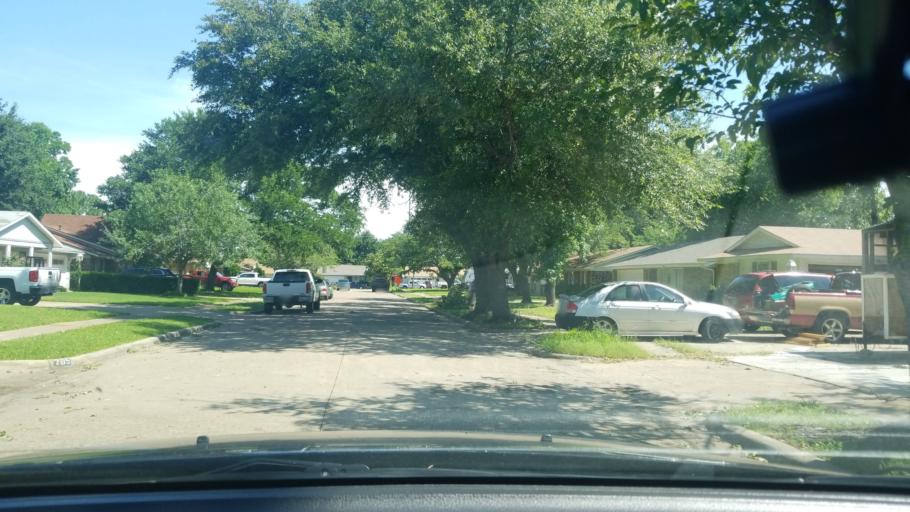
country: US
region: Texas
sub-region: Dallas County
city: Mesquite
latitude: 32.7739
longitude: -96.5951
